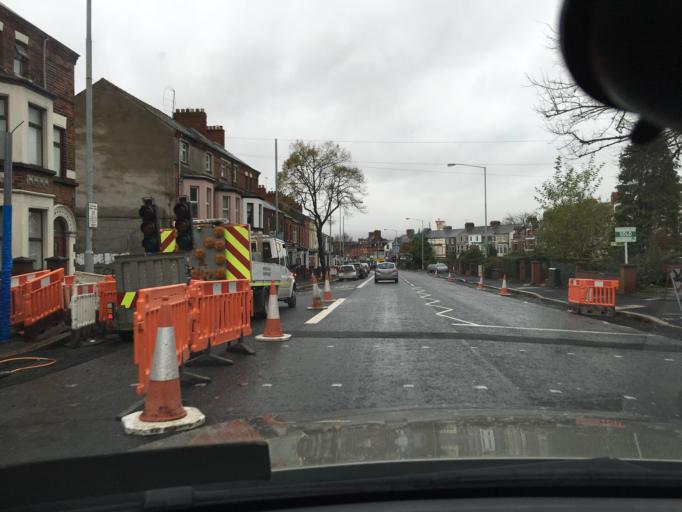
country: GB
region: Northern Ireland
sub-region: Castlereagh District
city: Castlereagh
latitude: 54.5966
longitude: -5.8833
